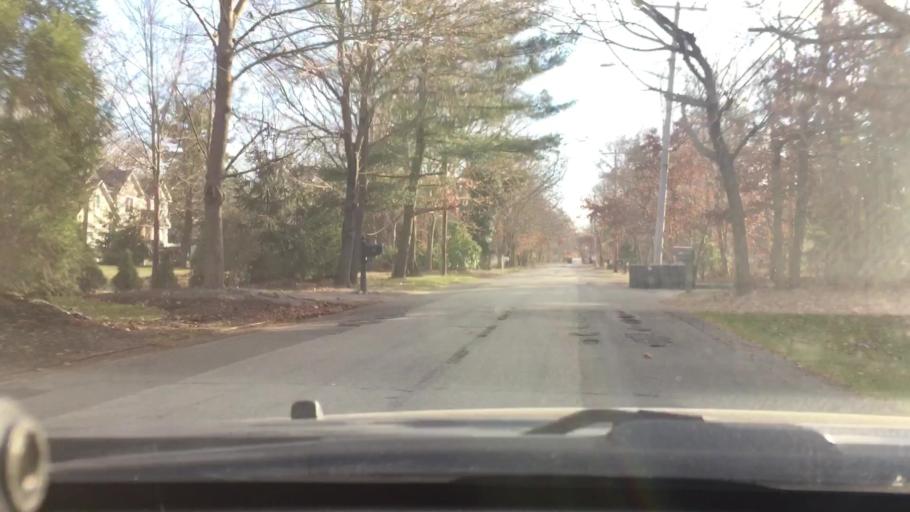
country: US
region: New York
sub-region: Suffolk County
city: Mount Sinai
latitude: 40.9188
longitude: -73.0141
